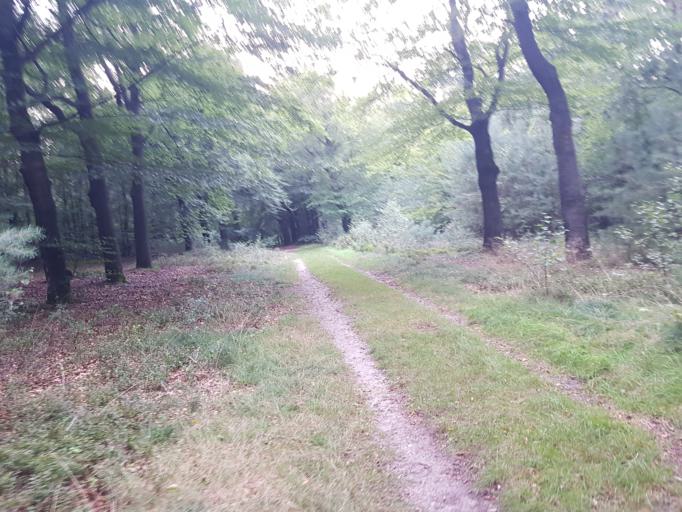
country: NL
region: Utrecht
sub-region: Gemeente Rhenen
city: Rhenen
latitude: 51.9846
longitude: 5.5508
